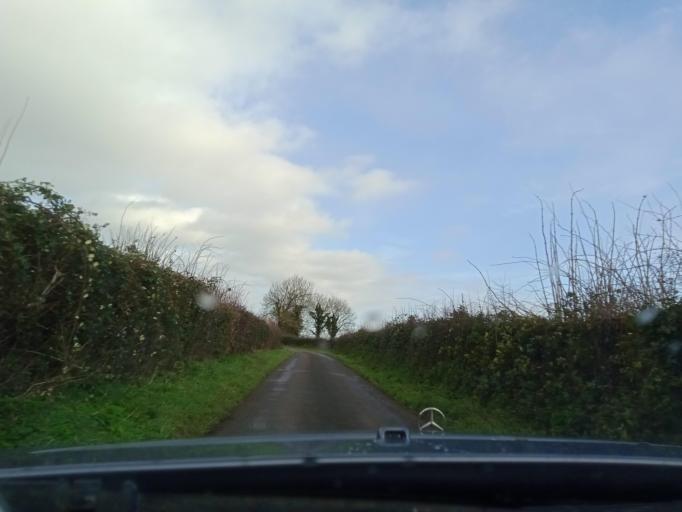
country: IE
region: Leinster
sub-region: Kilkenny
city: Callan
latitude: 52.4869
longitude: -7.3638
